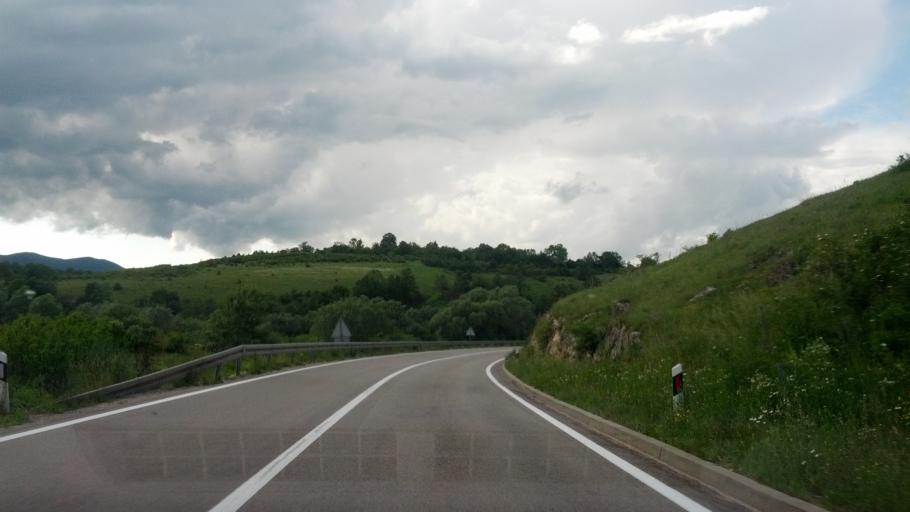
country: BA
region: Federation of Bosnia and Herzegovina
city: Izacic
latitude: 44.9174
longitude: 15.7145
